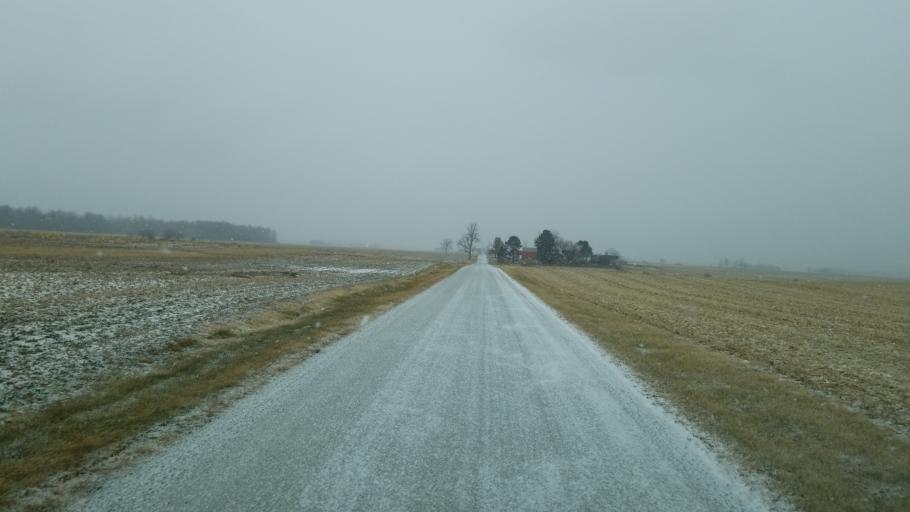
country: US
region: Ohio
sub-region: Hardin County
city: Kenton
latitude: 40.6845
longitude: -83.5475
